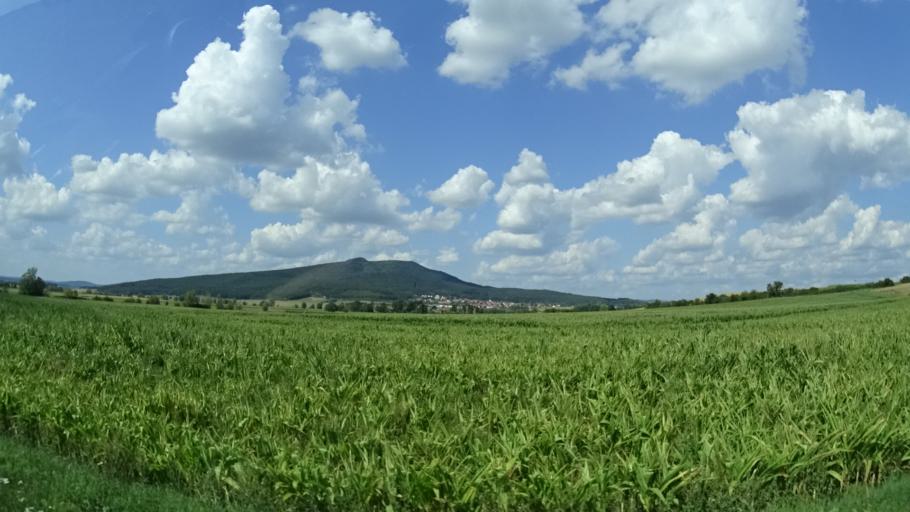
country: DE
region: Thuringia
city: Gleichamberg
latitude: 50.3462
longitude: 10.5943
